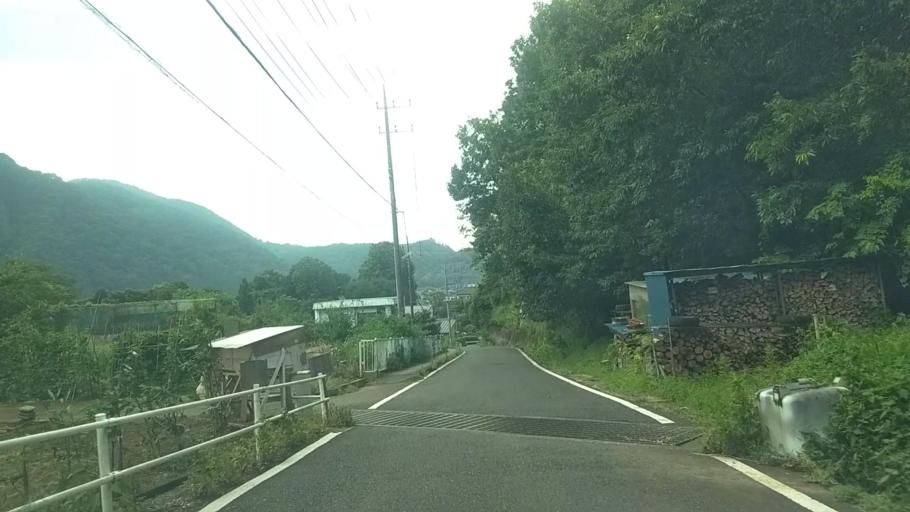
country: JP
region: Shizuoka
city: Mishima
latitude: 34.9984
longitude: 138.9446
